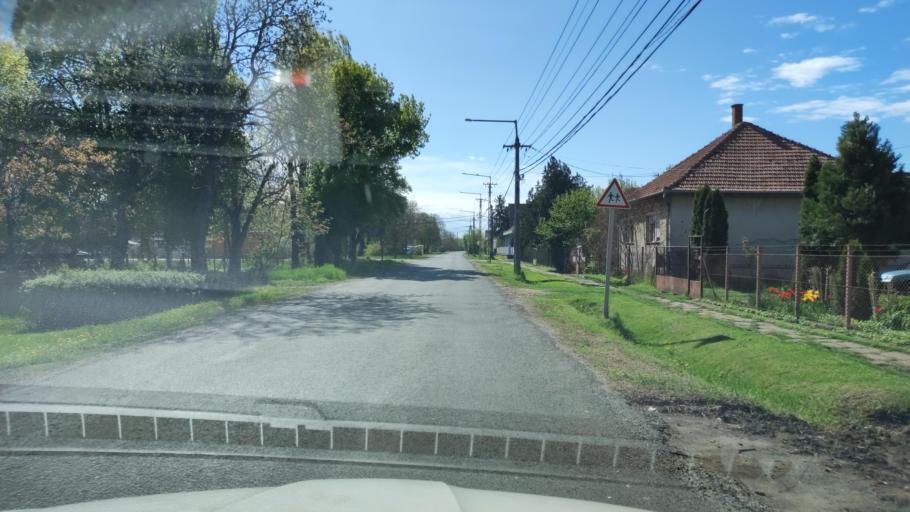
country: HU
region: Pest
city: Abony
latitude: 47.1776
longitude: 20.0133
